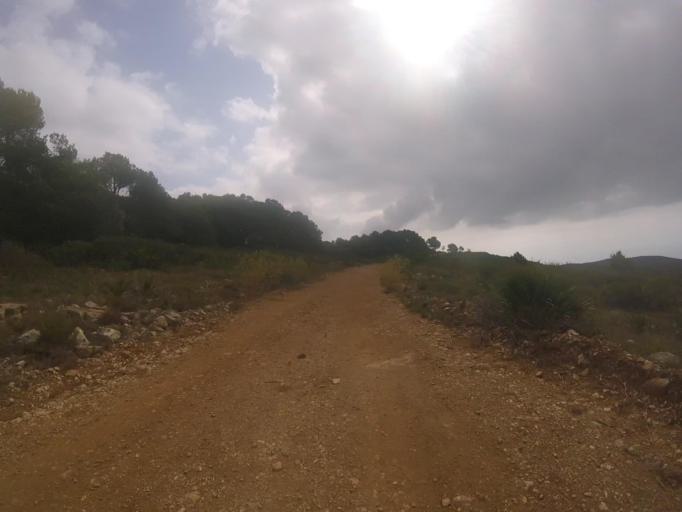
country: ES
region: Valencia
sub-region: Provincia de Castello
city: Santa Magdalena de Pulpis
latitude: 40.3494
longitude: 0.3309
